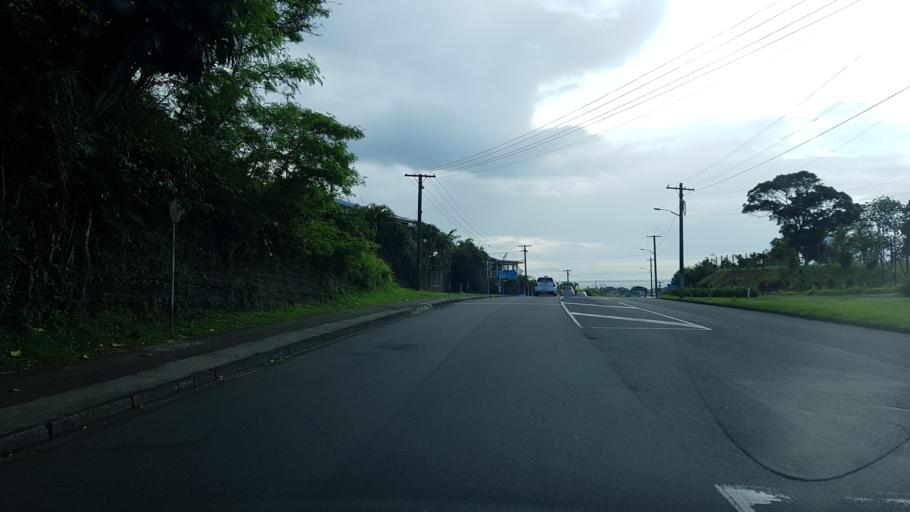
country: FJ
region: Central
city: Suva
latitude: -18.1454
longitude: 178.4408
